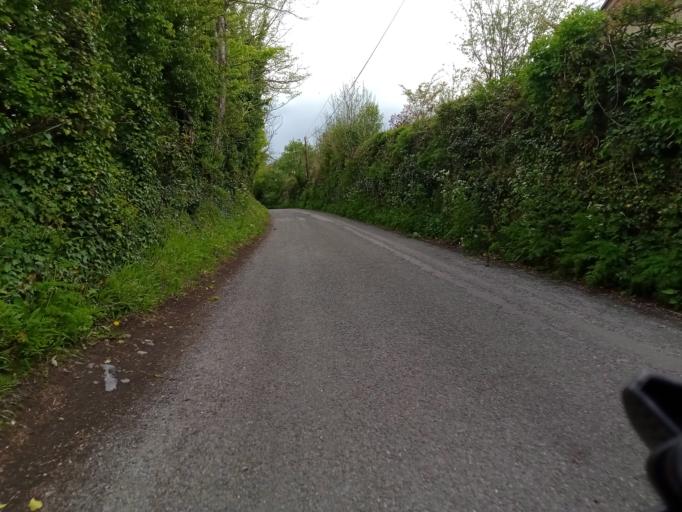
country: IE
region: Leinster
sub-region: Kilkenny
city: Kilkenny
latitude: 52.6735
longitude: -7.2584
